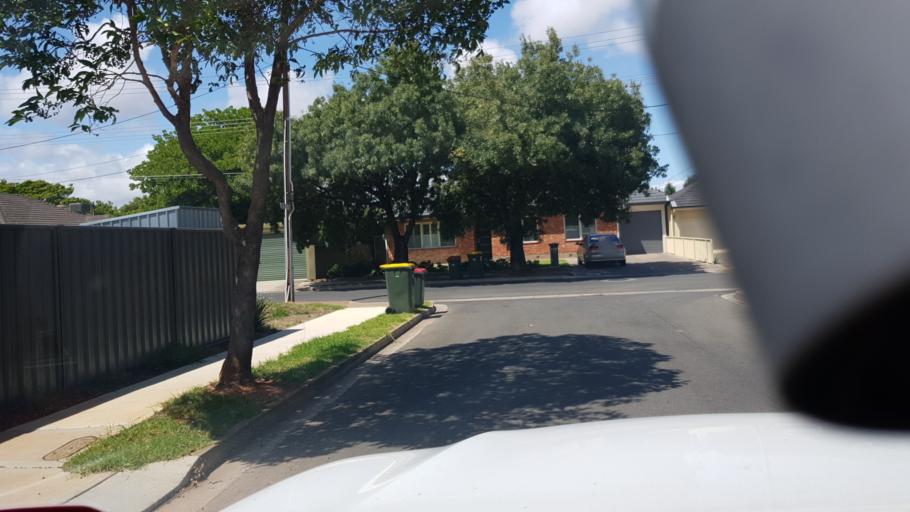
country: AU
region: South Australia
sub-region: Adelaide
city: Brighton
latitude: -35.0129
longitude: 138.5297
